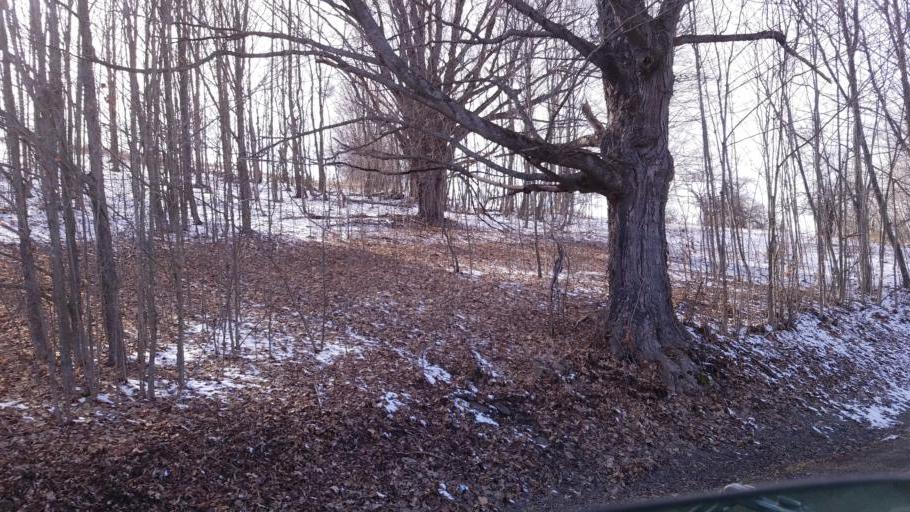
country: US
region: New York
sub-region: Allegany County
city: Wellsville
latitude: 42.0835
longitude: -78.0126
